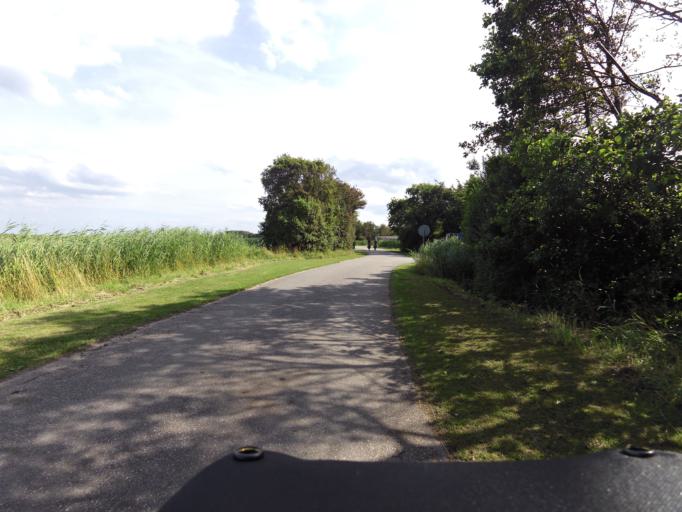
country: NL
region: South Holland
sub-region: Gemeente Goeree-Overflakkee
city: Ouddorp
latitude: 51.8047
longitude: 3.8640
